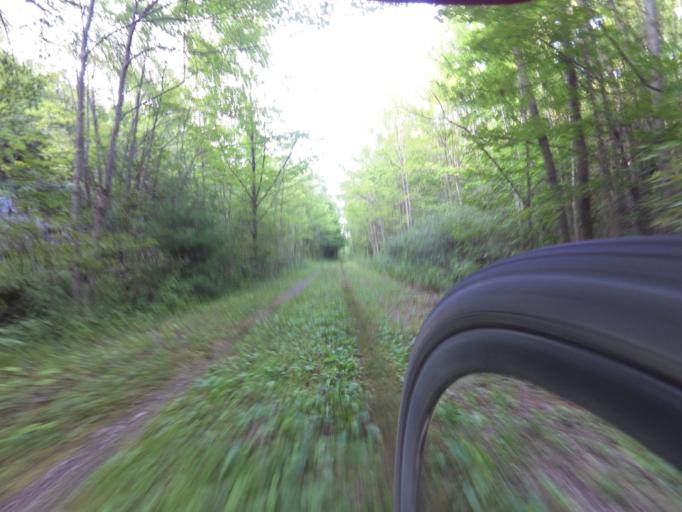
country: CA
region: Ontario
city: Gananoque
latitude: 44.5347
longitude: -76.4053
